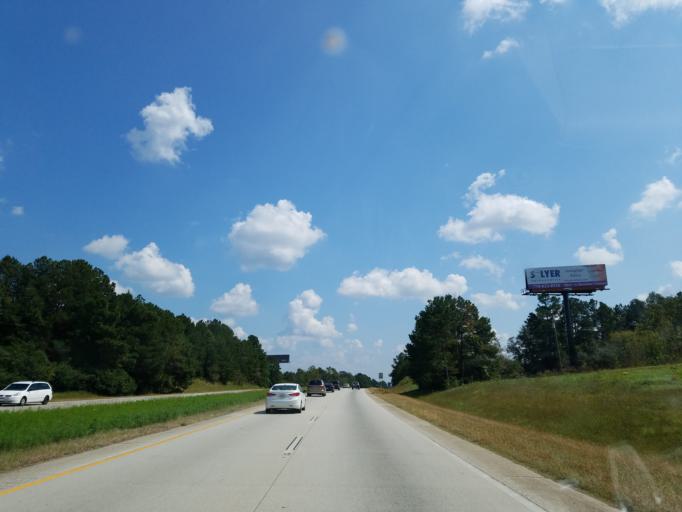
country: US
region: Georgia
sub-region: Barrow County
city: Winder
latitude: 33.9518
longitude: -83.7647
